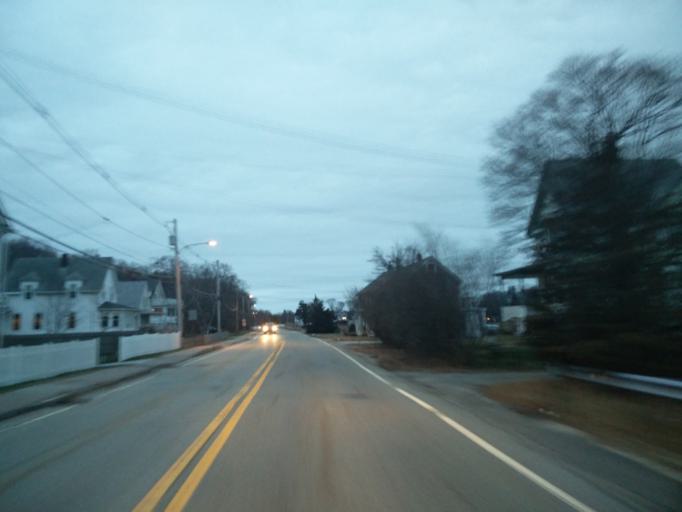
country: US
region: Massachusetts
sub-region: Norfolk County
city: Cohasset
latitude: 42.2592
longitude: -70.8462
